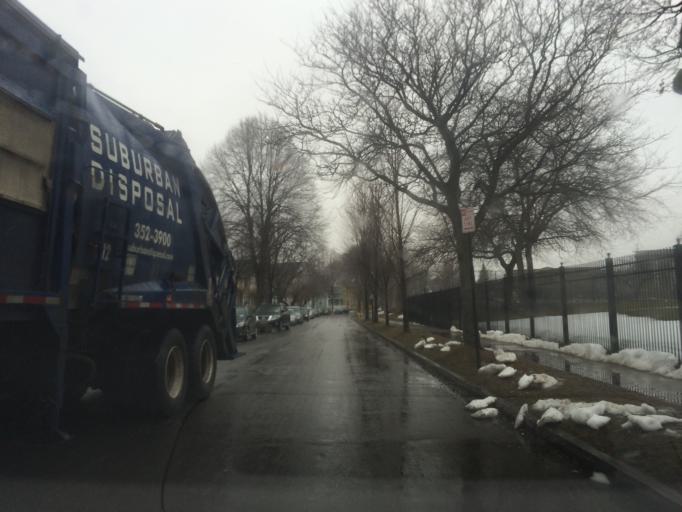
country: US
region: New York
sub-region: Monroe County
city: Rochester
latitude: 43.1478
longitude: -77.5957
